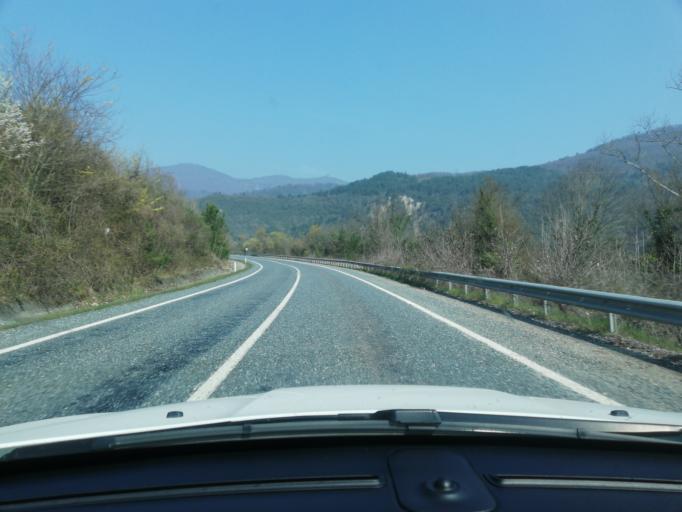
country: TR
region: Zonguldak
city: Gokcebey
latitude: 41.2288
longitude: 32.2140
